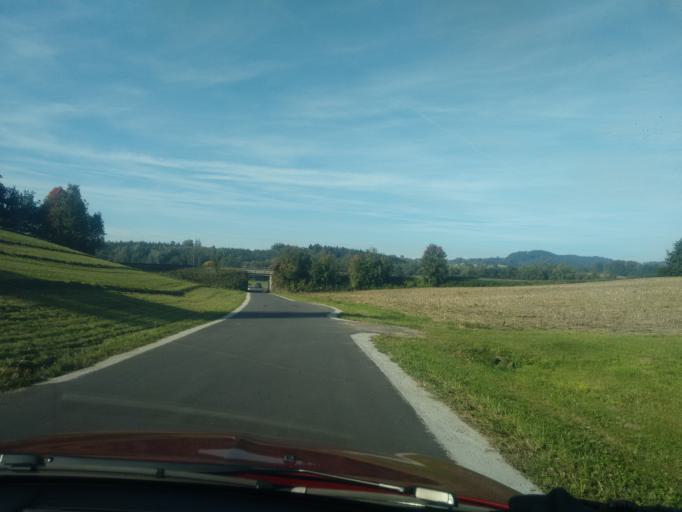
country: AT
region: Upper Austria
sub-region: Politischer Bezirk Vocklabruck
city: Manning
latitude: 48.0686
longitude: 13.6702
